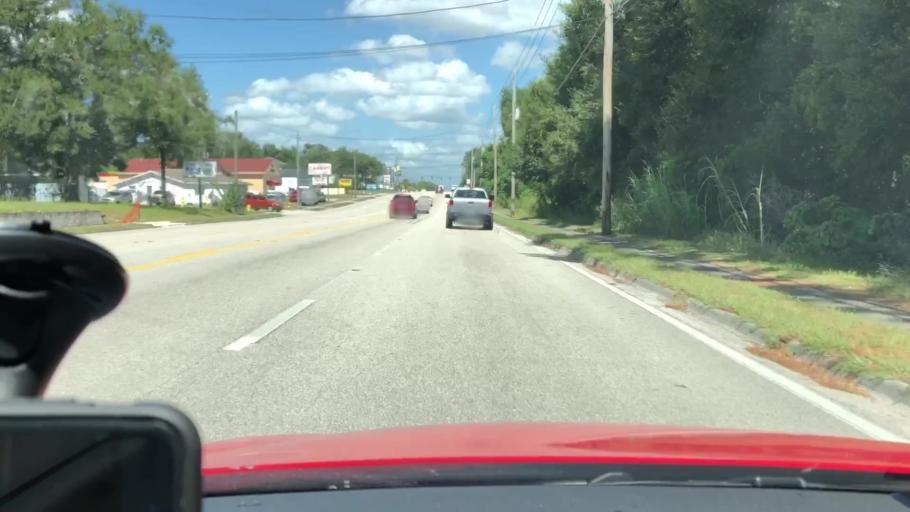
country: US
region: Florida
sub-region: Volusia County
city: West DeLand
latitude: 29.0178
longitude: -81.3238
